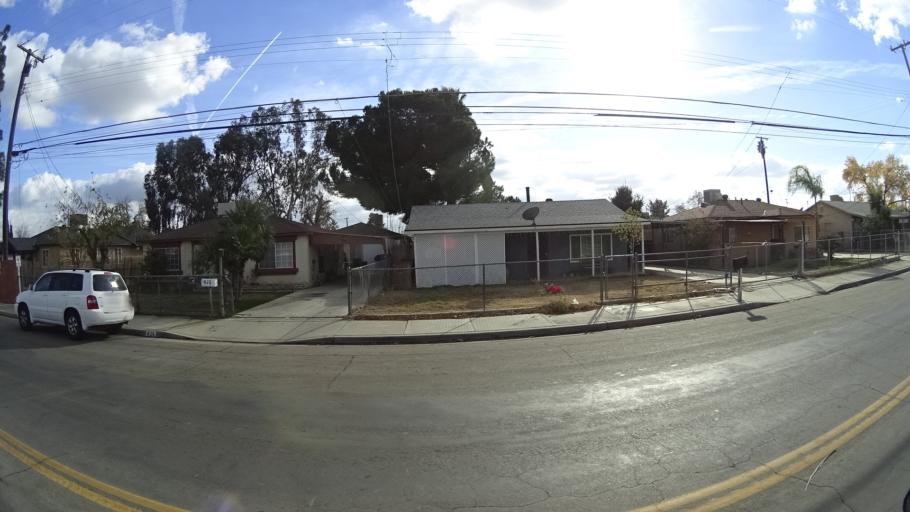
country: US
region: California
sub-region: Kern County
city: Bakersfield
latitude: 35.3322
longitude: -119.0112
